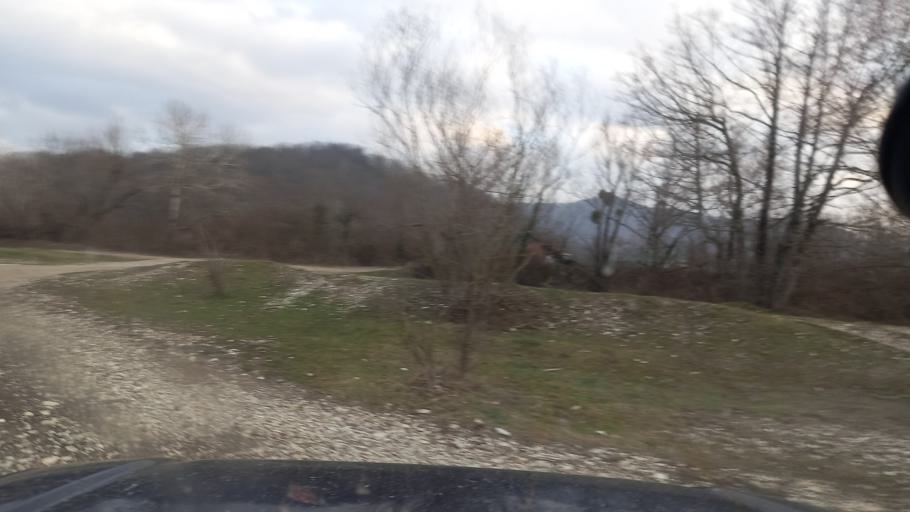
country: RU
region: Krasnodarskiy
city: Pshada
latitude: 44.4820
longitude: 38.4035
